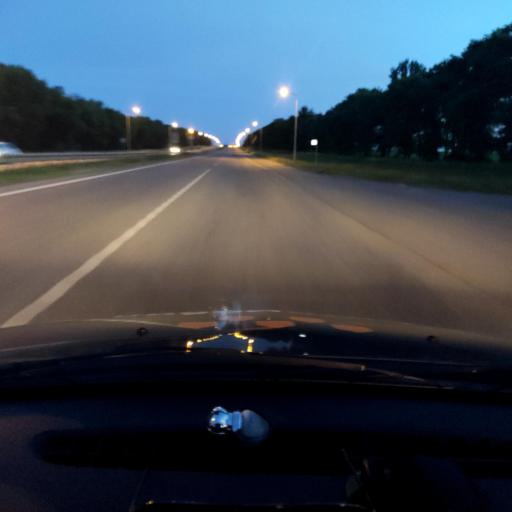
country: RU
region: Belgorod
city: Gubkin
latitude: 51.2495
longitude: 37.5228
